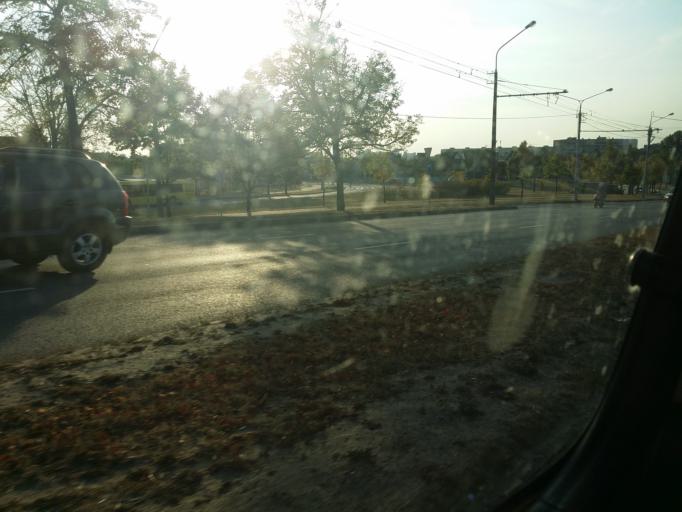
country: BY
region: Minsk
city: Minsk
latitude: 53.9051
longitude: 27.6342
